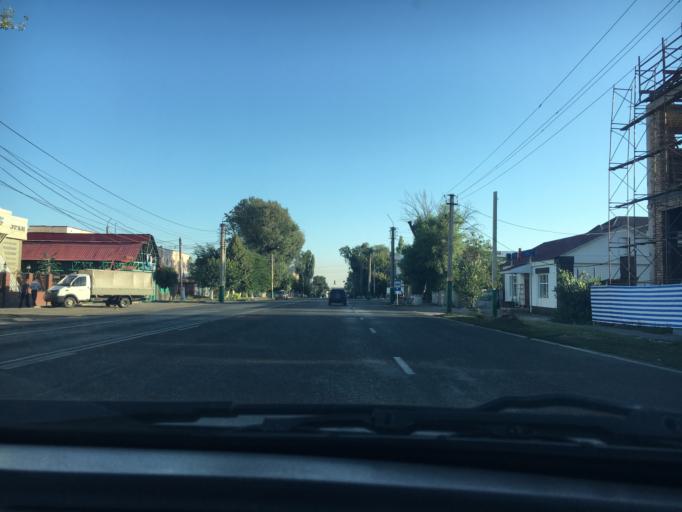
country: KZ
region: Zhambyl
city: Taraz
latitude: 42.8950
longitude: 71.3605
